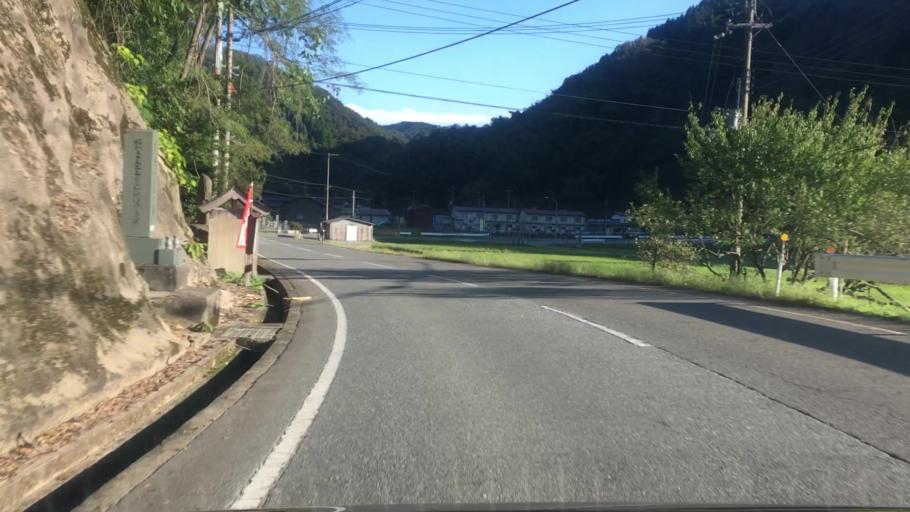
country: JP
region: Hyogo
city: Toyooka
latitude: 35.6070
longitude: 134.8073
